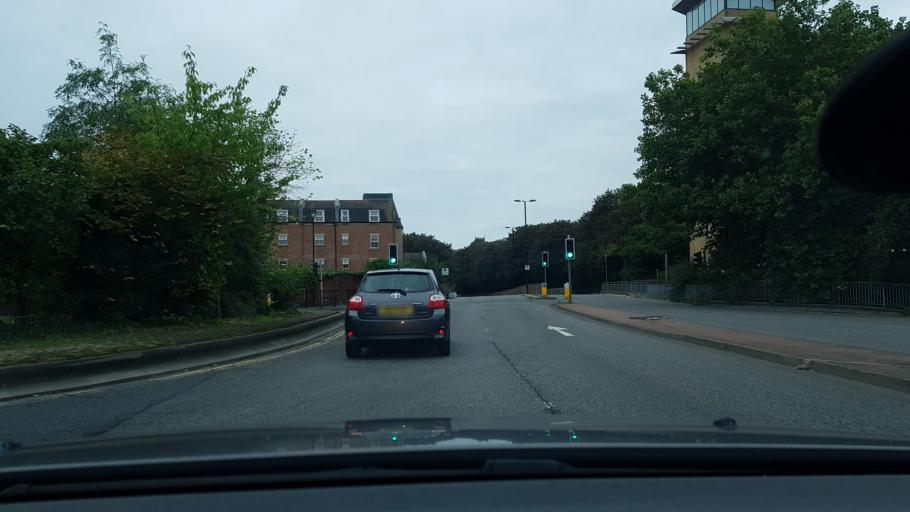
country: GB
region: England
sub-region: Southampton
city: Southampton
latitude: 50.9076
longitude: -1.3977
